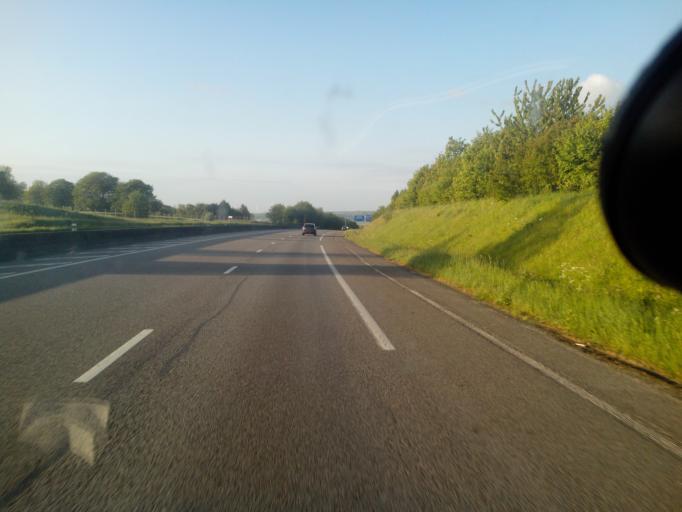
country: FR
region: Haute-Normandie
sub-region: Departement de la Seine-Maritime
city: Neufchatel-en-Bray
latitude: 49.7440
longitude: 1.4742
